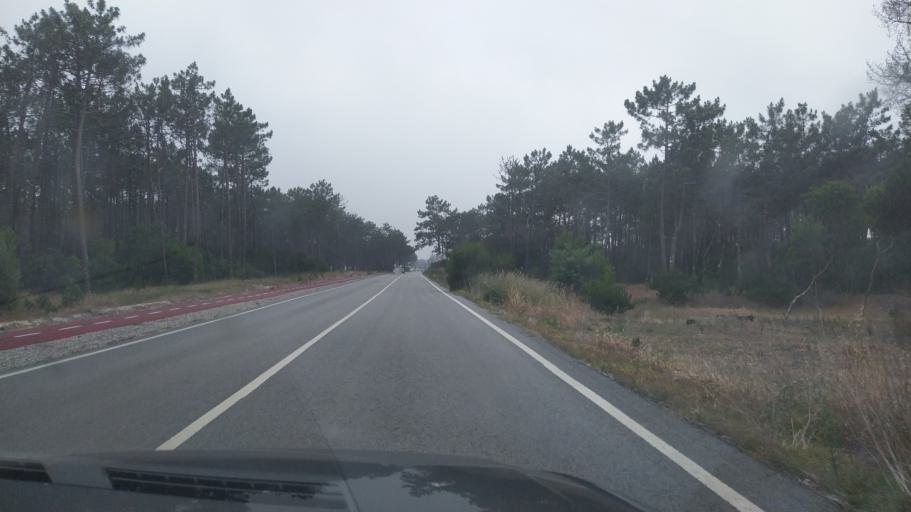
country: PT
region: Aveiro
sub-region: Ilhavo
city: Gafanha da Encarnacao
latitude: 40.5623
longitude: -8.7426
